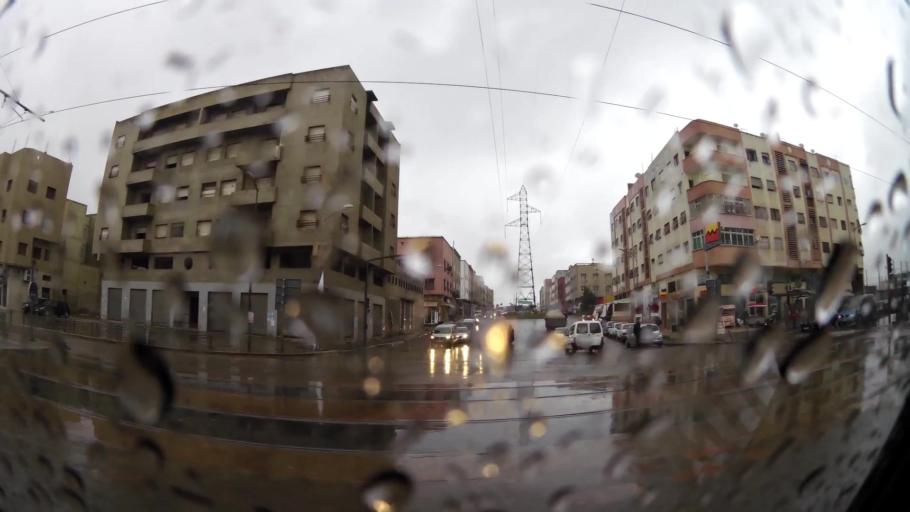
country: MA
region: Grand Casablanca
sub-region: Mediouna
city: Tit Mellil
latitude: 33.5761
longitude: -7.5183
